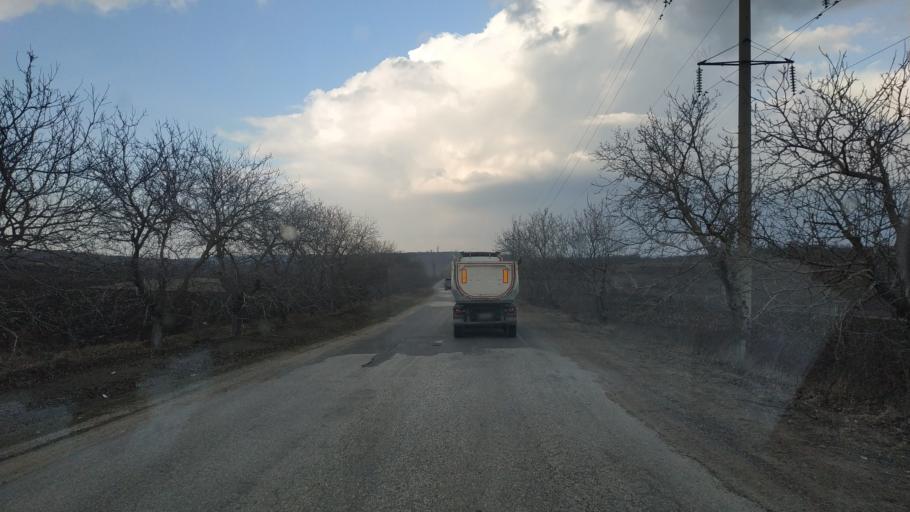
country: MD
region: Anenii Noi
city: Anenii Noi
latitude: 46.9737
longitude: 29.2852
